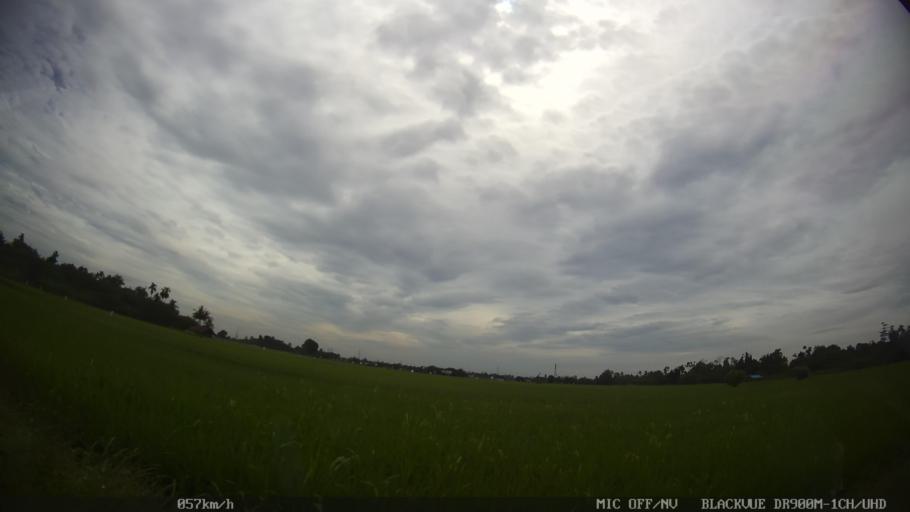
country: ID
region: North Sumatra
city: Sunggal
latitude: 3.5774
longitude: 98.5772
